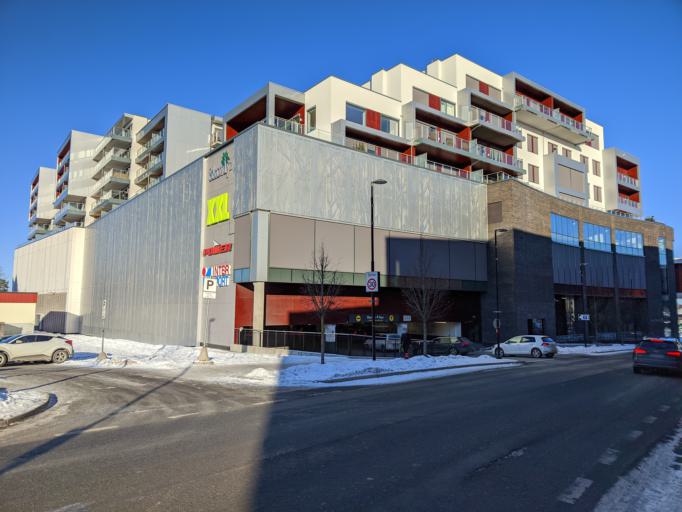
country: NO
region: Akershus
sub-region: Ullensaker
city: Jessheim
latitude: 60.1434
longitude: 11.1701
